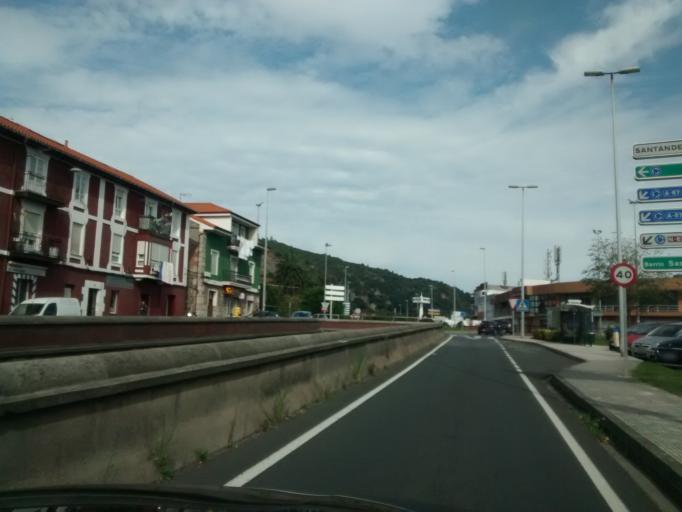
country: ES
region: Cantabria
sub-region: Provincia de Cantabria
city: Camargo
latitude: 43.4431
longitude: -3.8573
